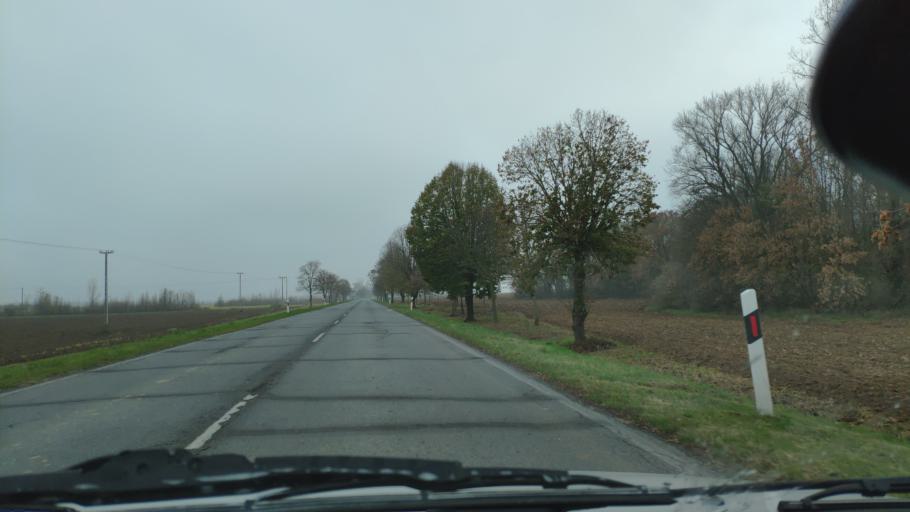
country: HU
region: Zala
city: Zalakomar
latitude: 46.5851
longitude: 17.2634
